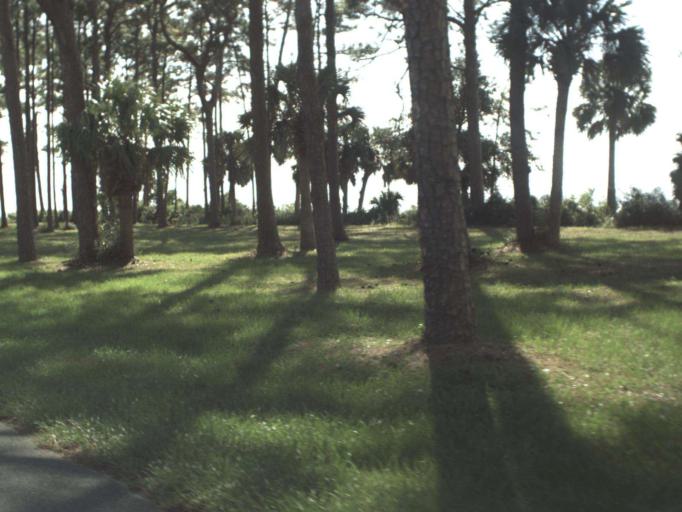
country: US
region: Florida
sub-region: Gulf County
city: Port Saint Joe
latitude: 29.7967
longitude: -85.3008
